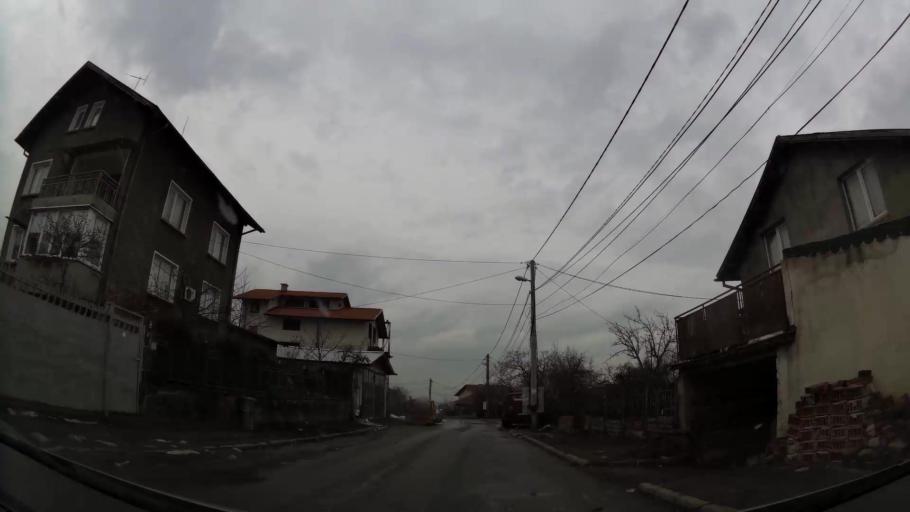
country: BG
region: Sofiya
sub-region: Obshtina Bozhurishte
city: Bozhurishte
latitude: 42.6949
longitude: 23.2218
